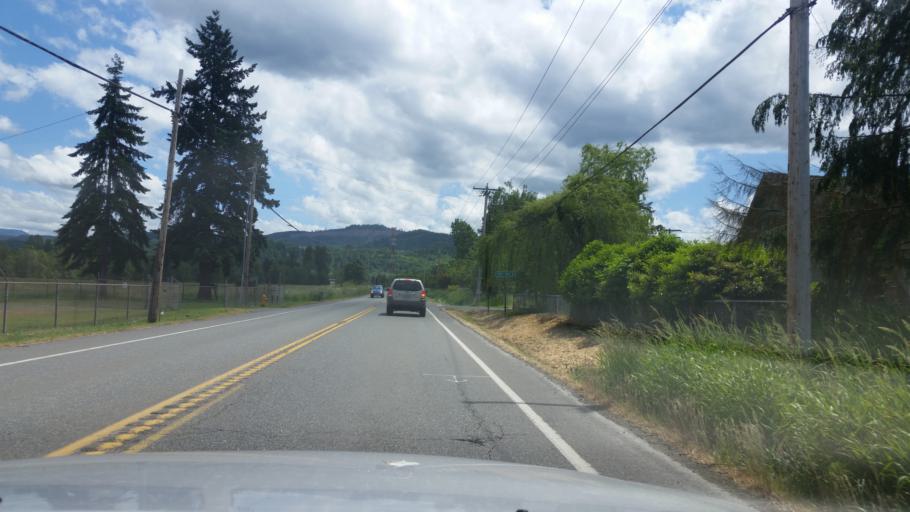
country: US
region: Washington
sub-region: Pierce County
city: Orting
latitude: 47.0862
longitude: -122.1936
